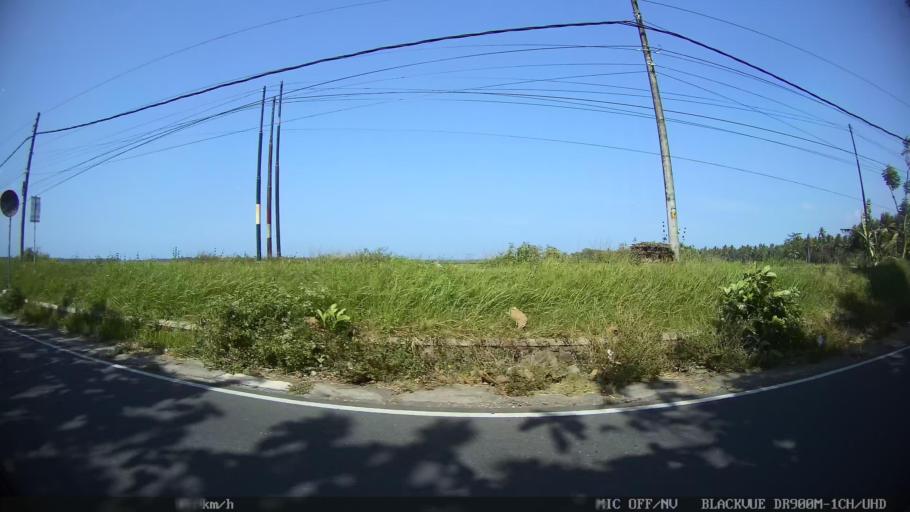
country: ID
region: Daerah Istimewa Yogyakarta
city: Srandakan
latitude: -7.9262
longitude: 110.1885
